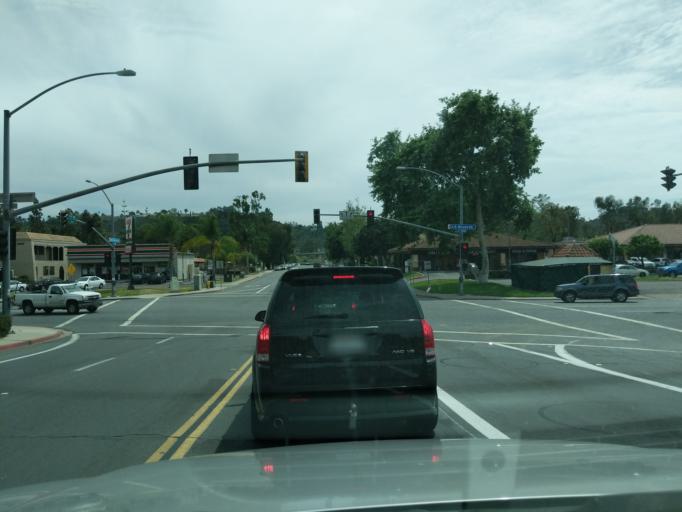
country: US
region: California
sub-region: San Diego County
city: San Diego
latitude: 32.7853
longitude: -117.1104
